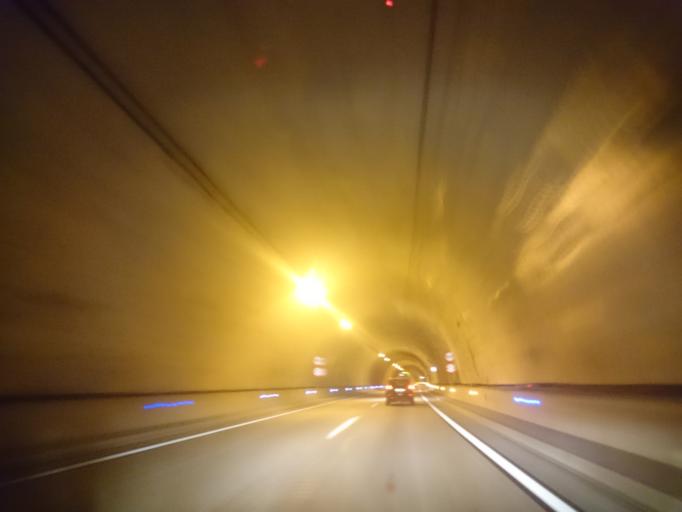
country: ES
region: Catalonia
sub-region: Provincia de Girona
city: Arbucies
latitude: 41.8497
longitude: 2.5216
